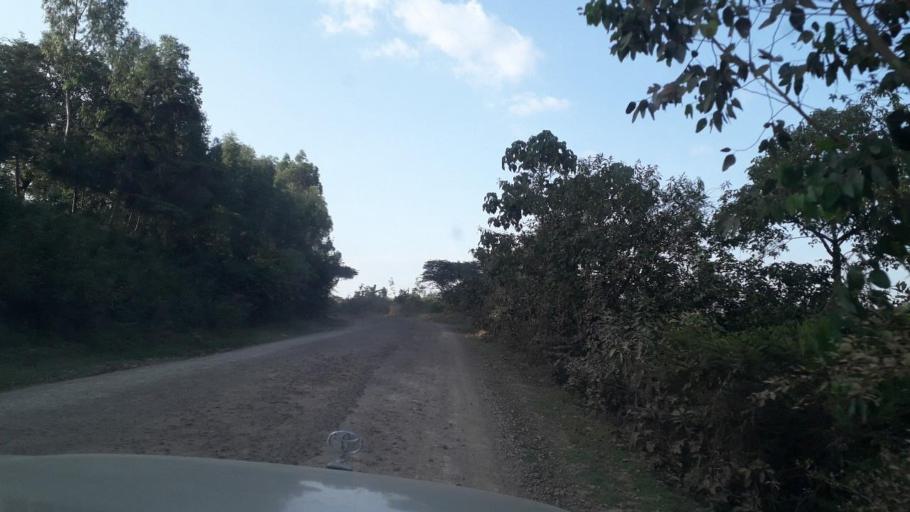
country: ET
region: Oromiya
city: Jima
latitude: 7.5874
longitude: 36.8572
